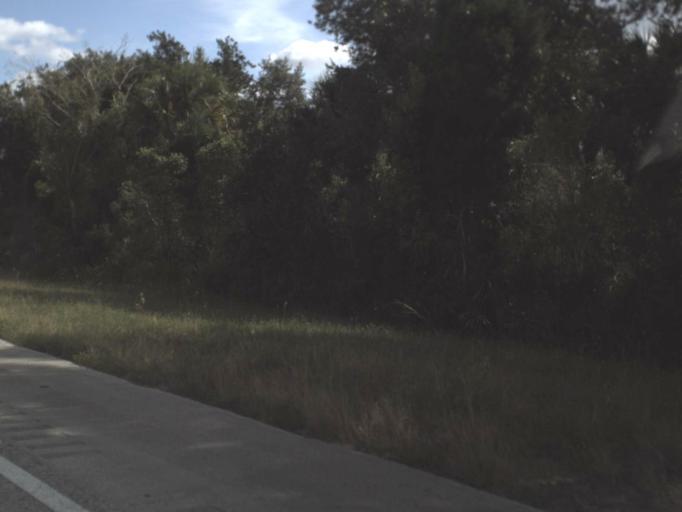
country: US
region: Florida
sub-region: Brevard County
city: Port Saint John
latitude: 28.4520
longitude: -80.8780
